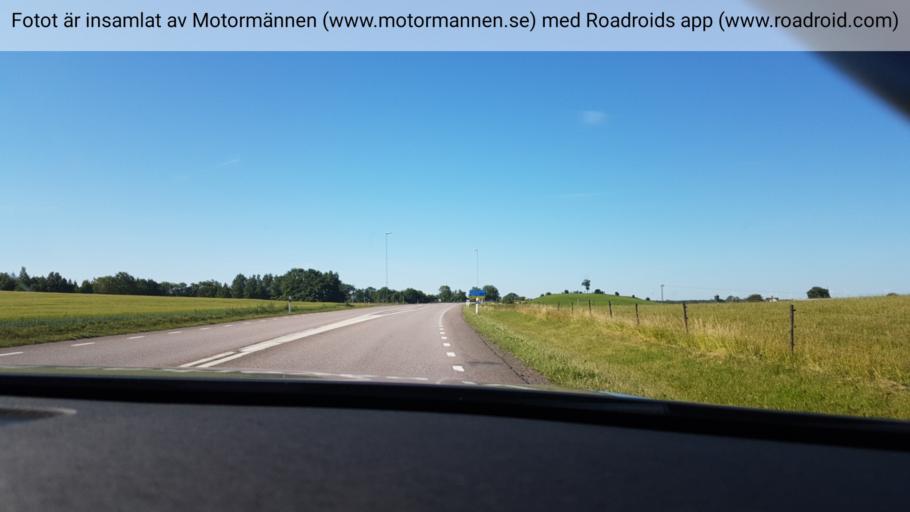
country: SE
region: Vaestra Goetaland
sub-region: Falkopings Kommun
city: Falkoeping
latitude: 58.1365
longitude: 13.5627
